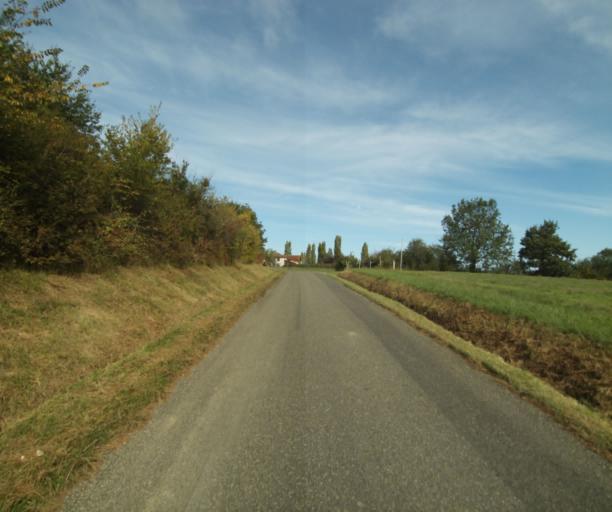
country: FR
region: Midi-Pyrenees
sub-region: Departement du Gers
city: Eauze
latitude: 43.9065
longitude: 0.1421
